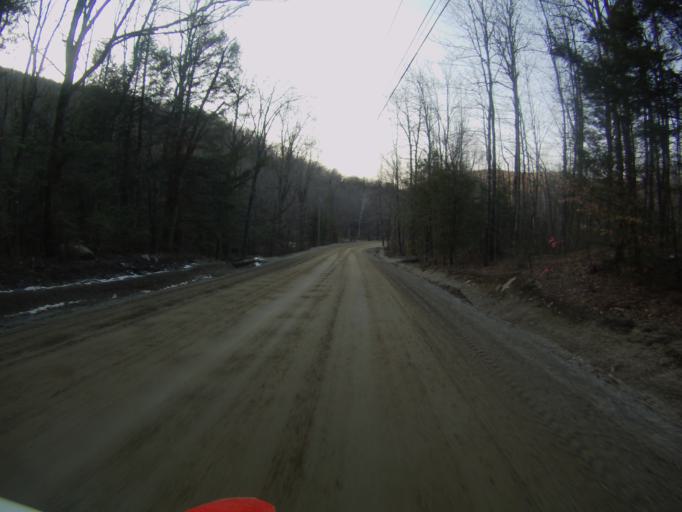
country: US
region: Vermont
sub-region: Addison County
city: Bristol
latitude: 44.0728
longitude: -73.0598
